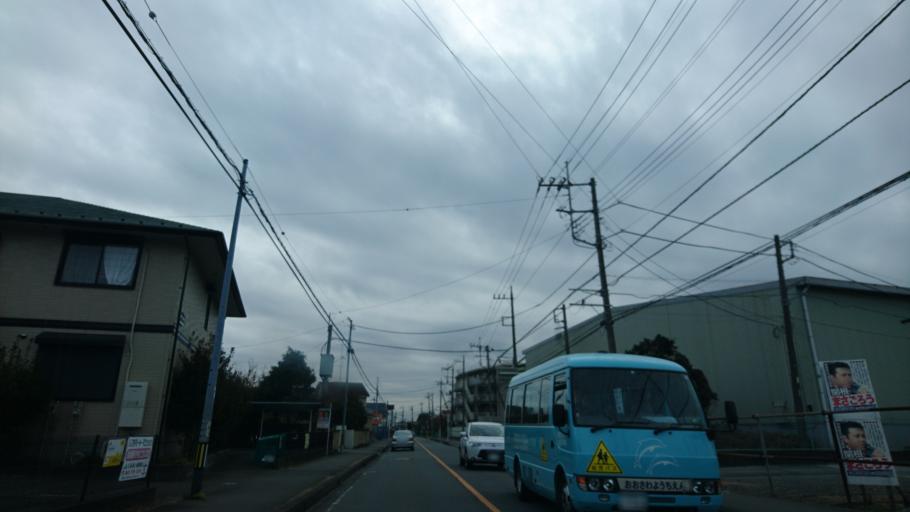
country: JP
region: Tokyo
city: Hachioji
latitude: 35.5782
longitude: 139.3348
